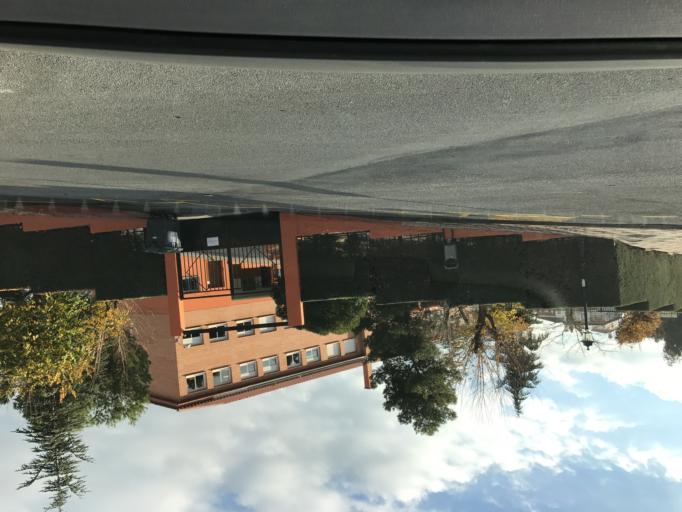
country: ES
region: Andalusia
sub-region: Provincia de Granada
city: Cajar
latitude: 37.1274
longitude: -3.5662
